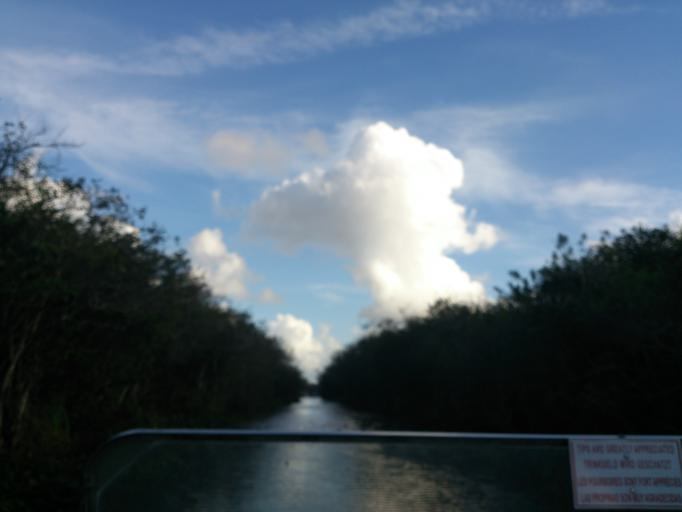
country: US
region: Florida
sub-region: Miami-Dade County
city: Kendall West
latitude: 25.7605
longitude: -80.5802
